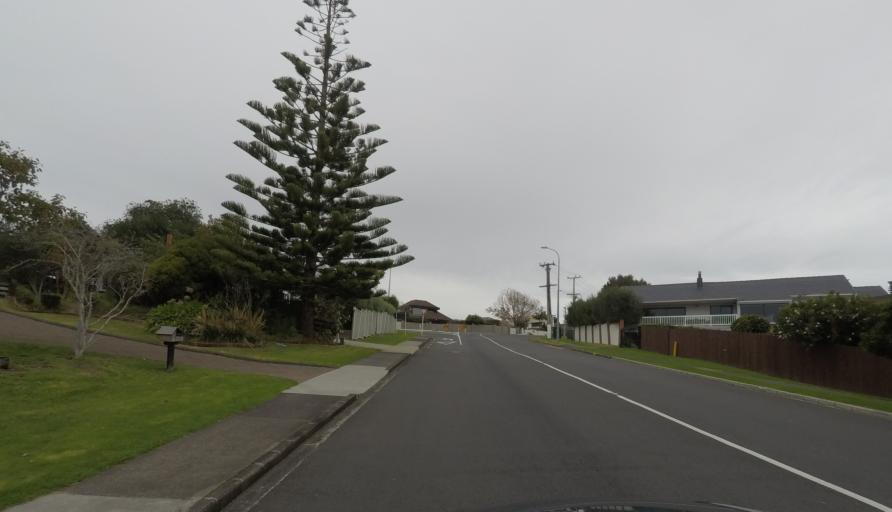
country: NZ
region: Auckland
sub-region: Auckland
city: Pakuranga
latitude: -36.8964
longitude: 174.9440
